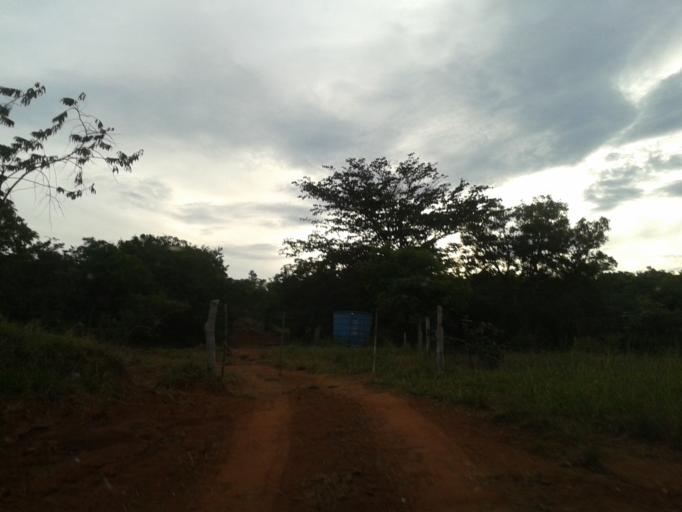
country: BR
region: Minas Gerais
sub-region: Campina Verde
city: Campina Verde
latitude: -19.4172
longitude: -49.6113
